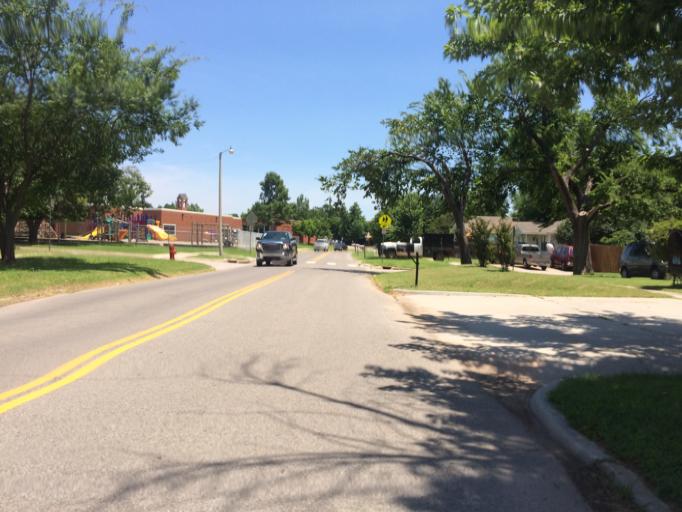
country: US
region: Oklahoma
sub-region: Cleveland County
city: Norman
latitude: 35.2252
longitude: -97.4360
